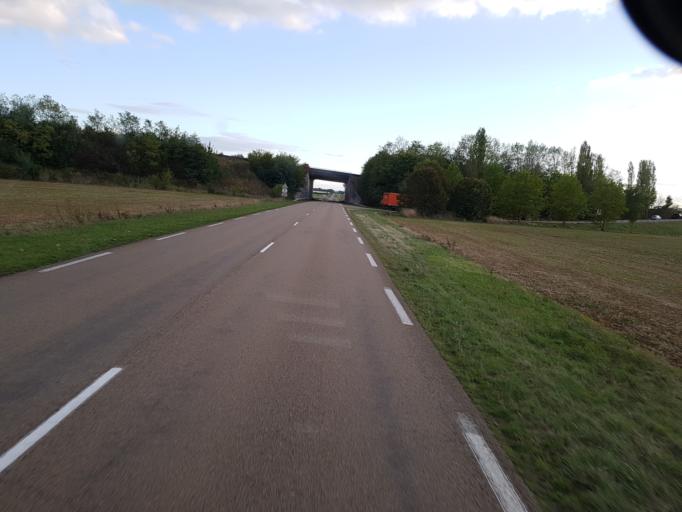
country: FR
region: Bourgogne
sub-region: Departement de l'Yonne
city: Soucy
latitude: 48.2586
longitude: 3.2833
